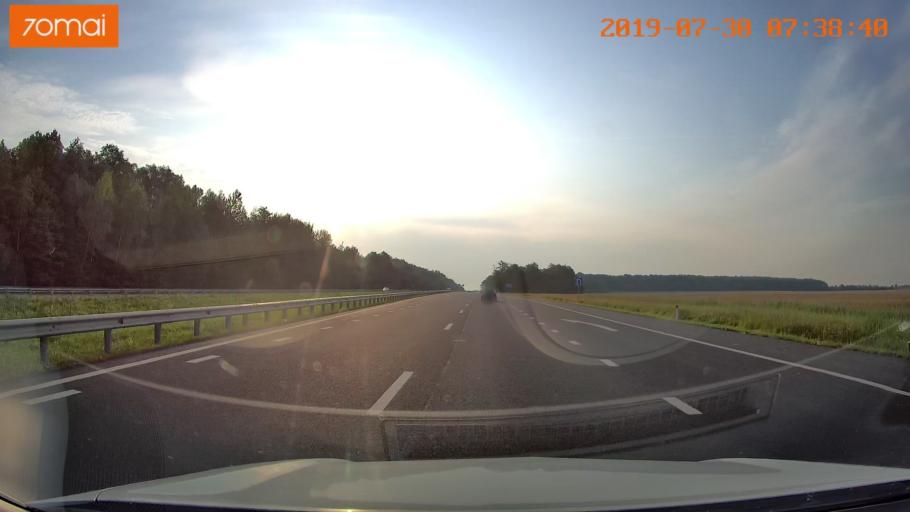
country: RU
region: Kaliningrad
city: Gvardeysk
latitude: 54.6498
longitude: 21.1745
